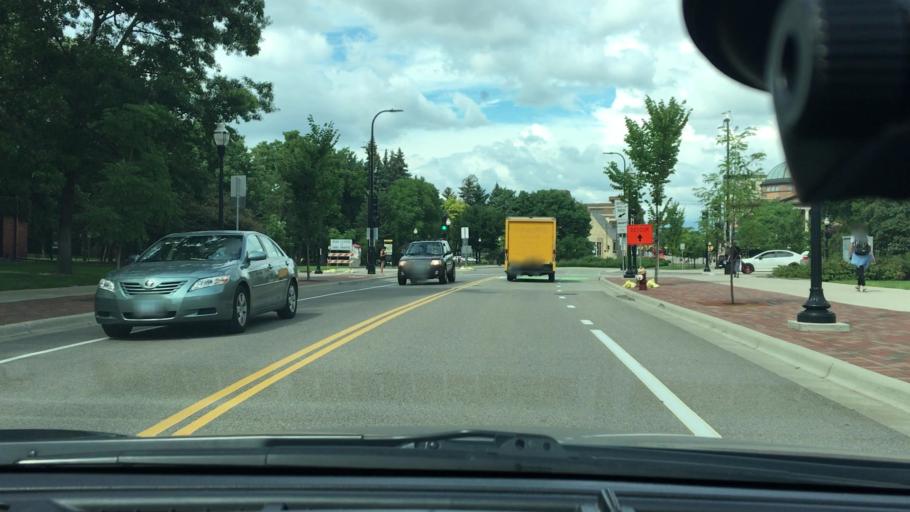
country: US
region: Minnesota
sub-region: Hennepin County
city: Minneapolis
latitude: 44.9773
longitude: -93.2364
